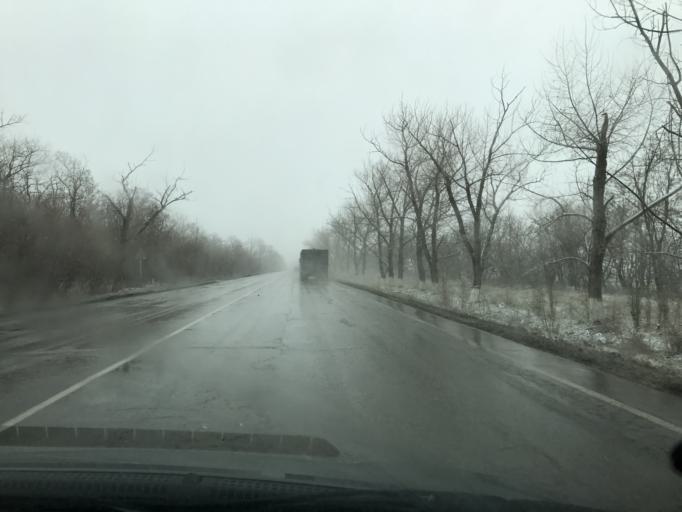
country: RU
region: Rostov
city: Bataysk
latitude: 47.0412
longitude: 39.8569
